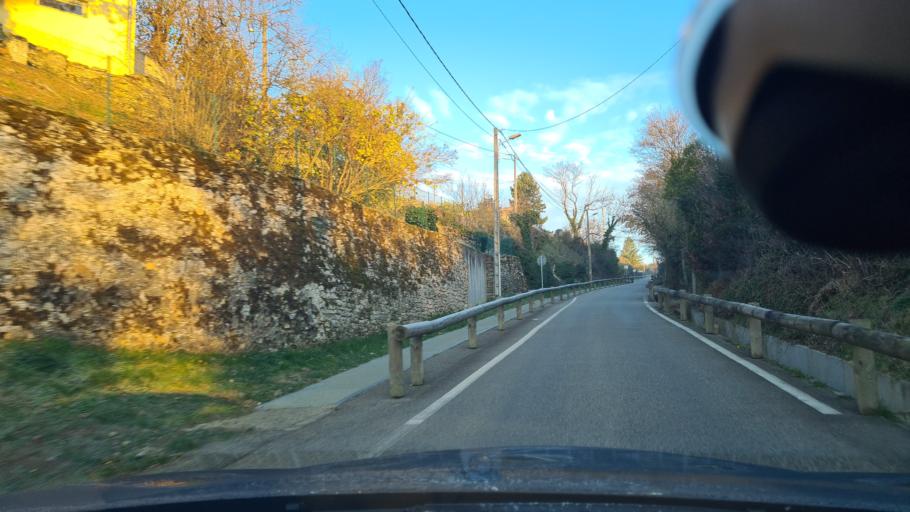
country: FR
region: Rhone-Alpes
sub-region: Departement du Rhone
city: Limonest
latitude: 45.8263
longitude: 4.7970
